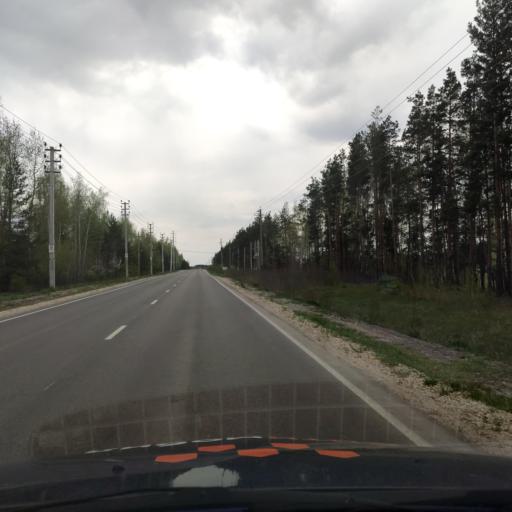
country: RU
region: Voronezj
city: Podgornoye
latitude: 51.8635
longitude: 39.1684
